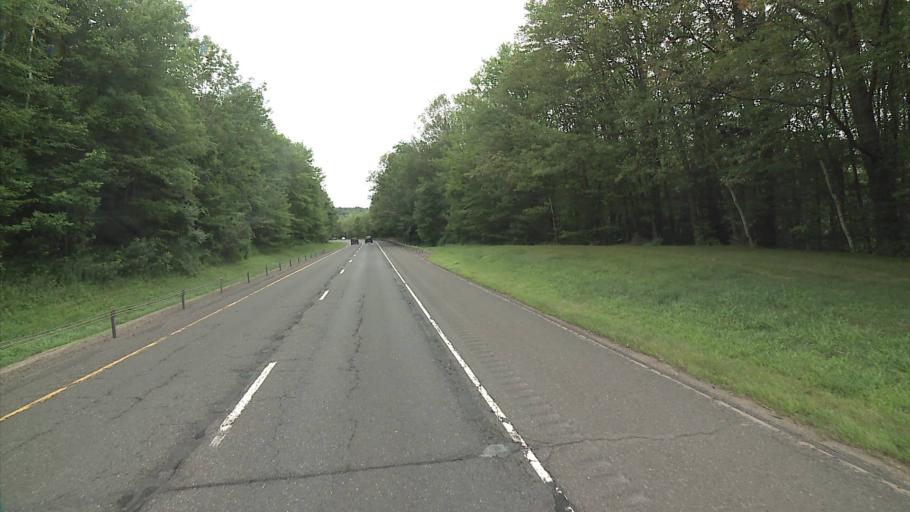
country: US
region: Connecticut
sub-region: Litchfield County
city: Oakville
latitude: 41.6250
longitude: -73.0700
